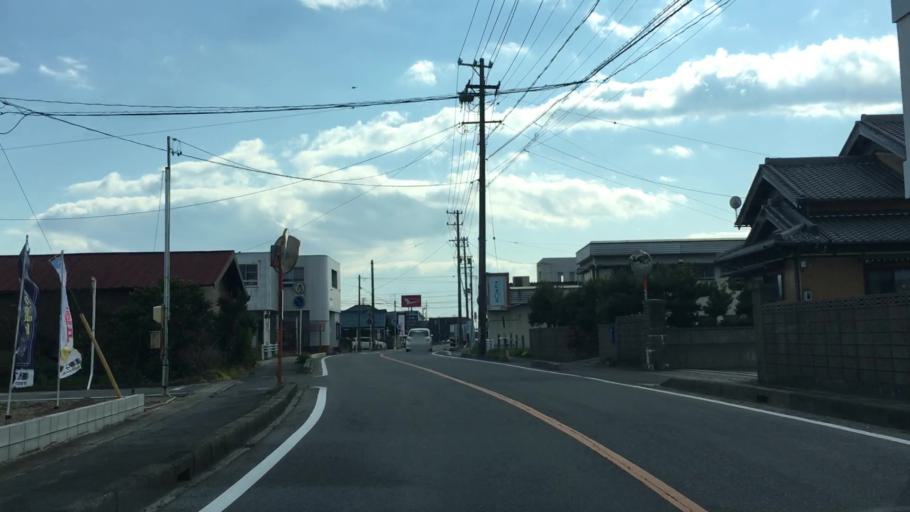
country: JP
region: Aichi
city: Ishiki
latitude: 34.7948
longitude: 137.0416
